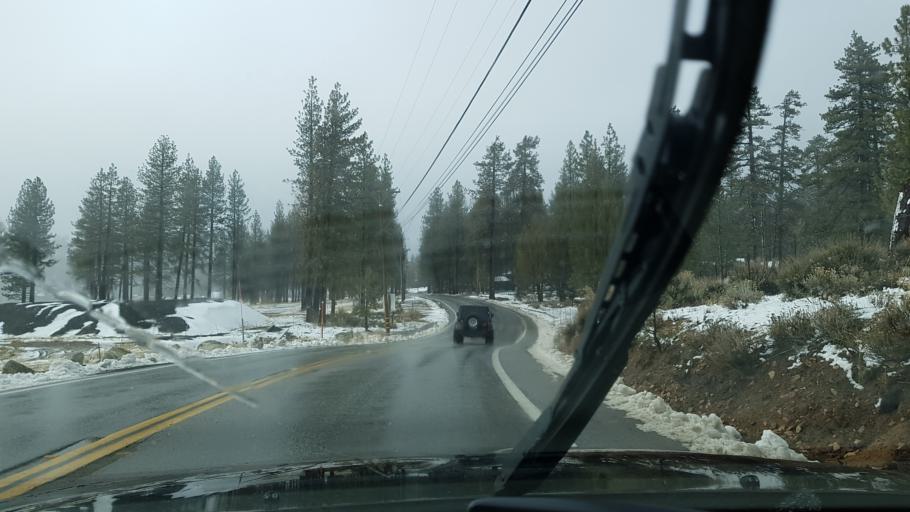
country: US
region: California
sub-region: San Bernardino County
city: Big Bear Lake
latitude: 34.2636
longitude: -116.9365
